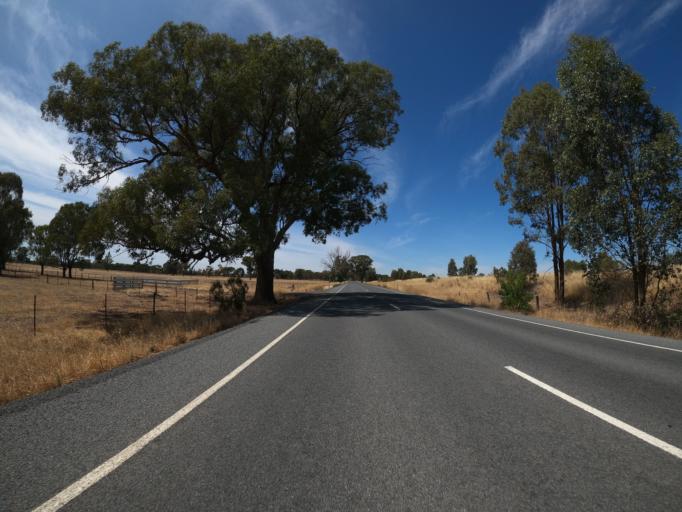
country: AU
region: Victoria
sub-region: Benalla
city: Benalla
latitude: -36.5196
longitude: 146.0344
